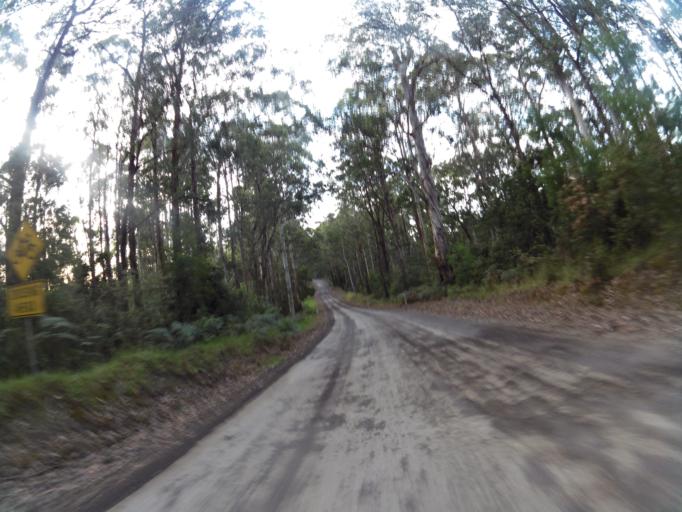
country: AU
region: Victoria
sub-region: Colac-Otway
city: Apollo Bay
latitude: -38.5404
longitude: 143.7298
